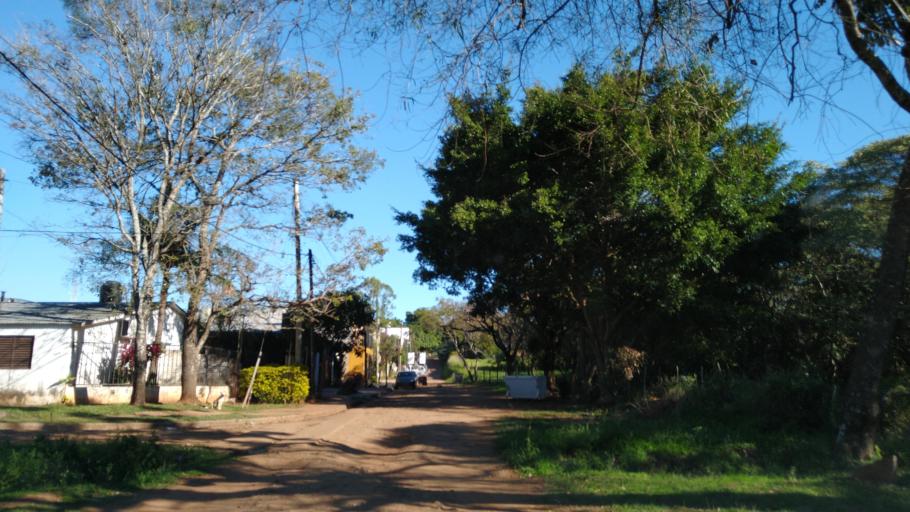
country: AR
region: Misiones
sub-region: Departamento de Capital
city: Posadas
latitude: -27.3624
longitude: -55.9292
